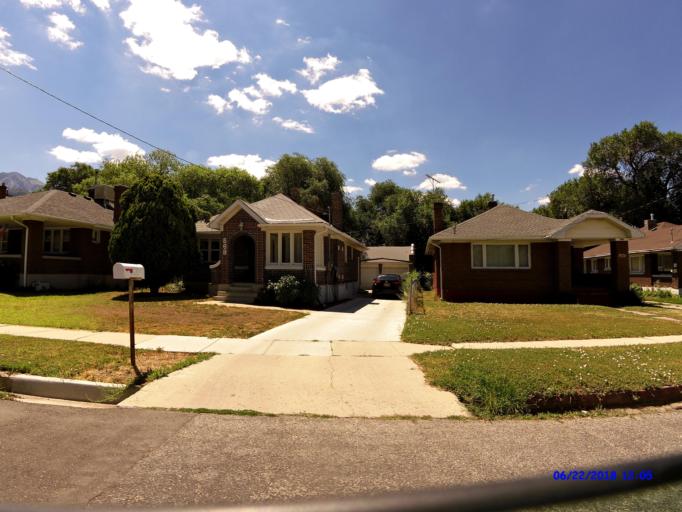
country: US
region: Utah
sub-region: Weber County
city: Ogden
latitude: 41.2381
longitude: -111.9570
